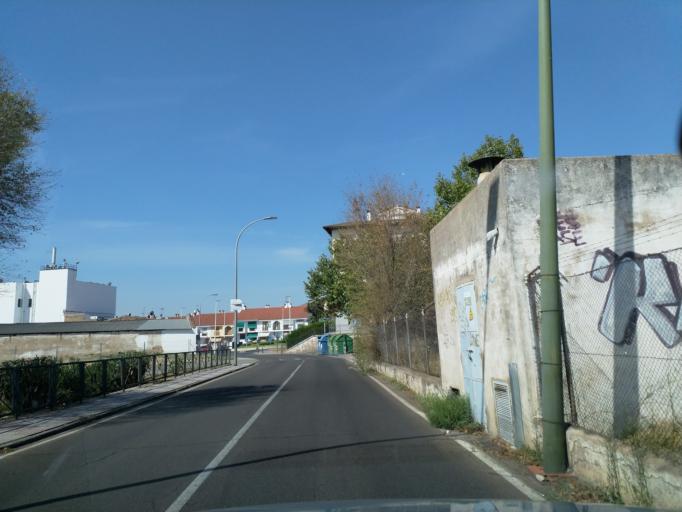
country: ES
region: Extremadura
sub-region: Provincia de Badajoz
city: Merida
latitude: 38.9254
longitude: -6.3471
